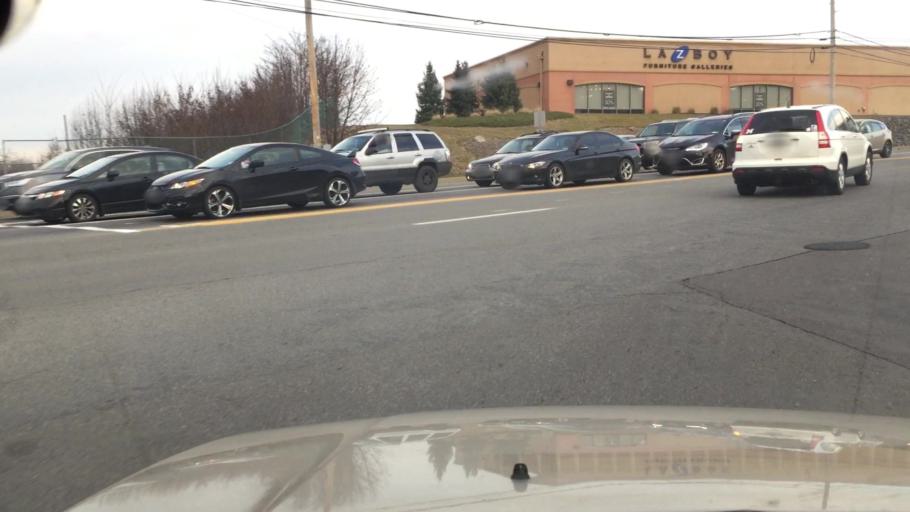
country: US
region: Pennsylvania
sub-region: Luzerne County
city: Georgetown
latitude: 41.2437
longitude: -75.8489
